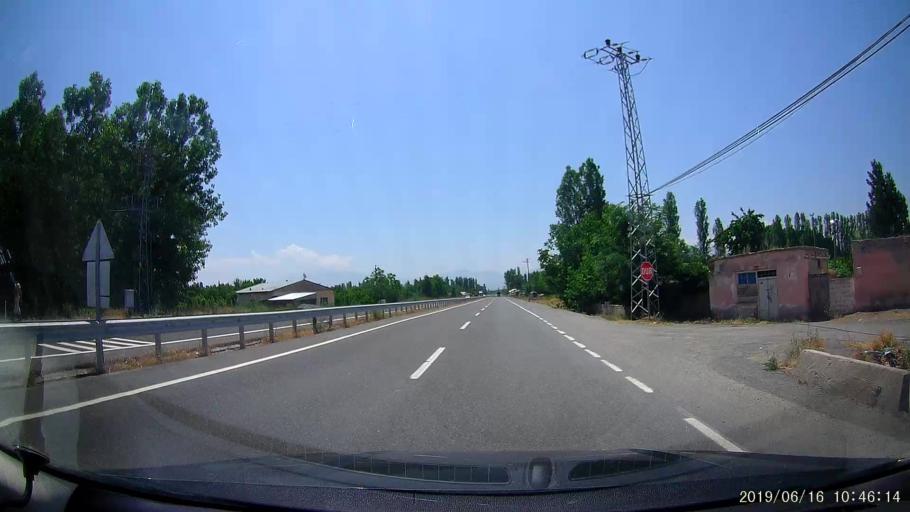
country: AM
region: Armavir
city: Shenavan
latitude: 40.0237
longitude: 43.8780
